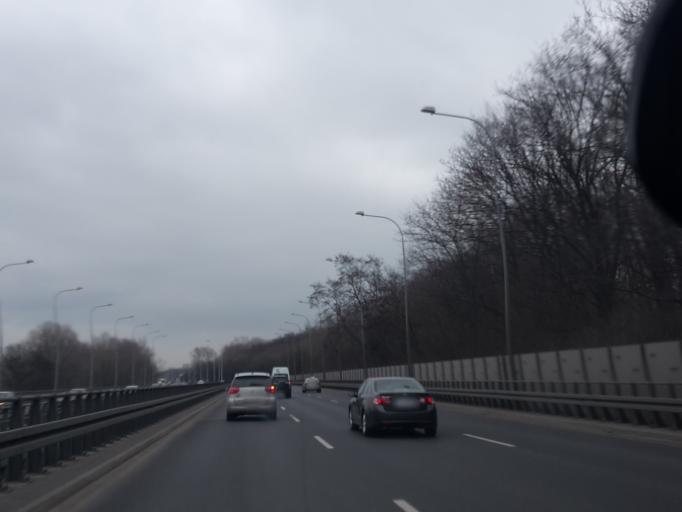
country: PL
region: Masovian Voivodeship
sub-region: Warszawa
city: Bielany
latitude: 52.2975
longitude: 20.9608
